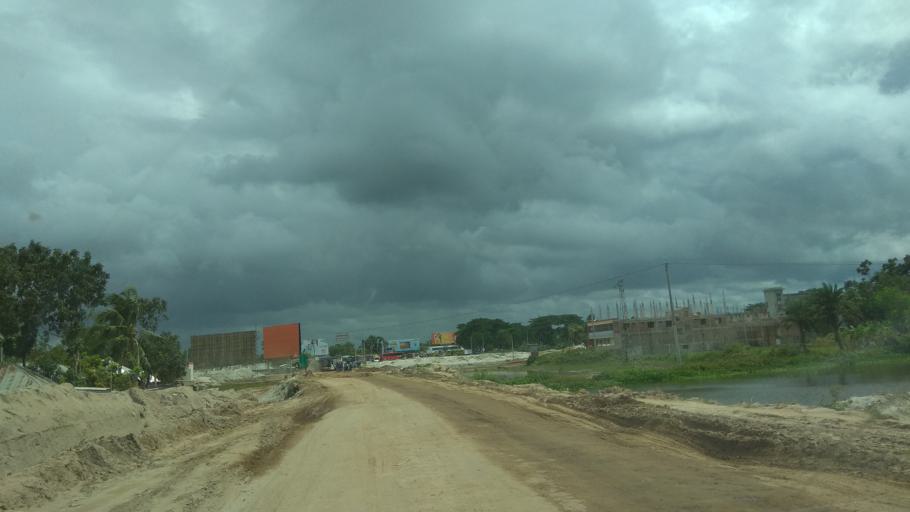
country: BD
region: Khulna
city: Kalia
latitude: 23.2110
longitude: 89.7091
